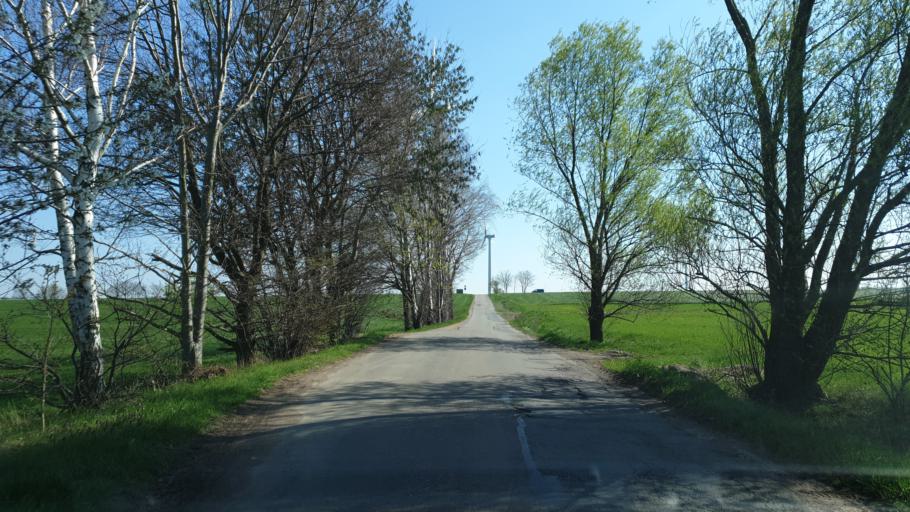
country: DE
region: Saxony
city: Hohndorf
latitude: 50.7672
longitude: 12.6840
